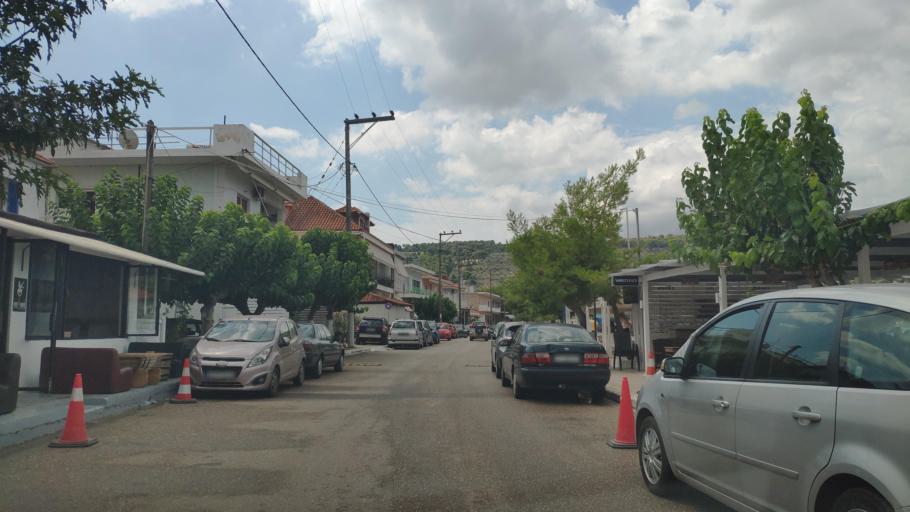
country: GR
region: Central Greece
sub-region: Nomos Fthiotidos
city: Malesina
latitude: 38.6545
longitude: 23.1928
